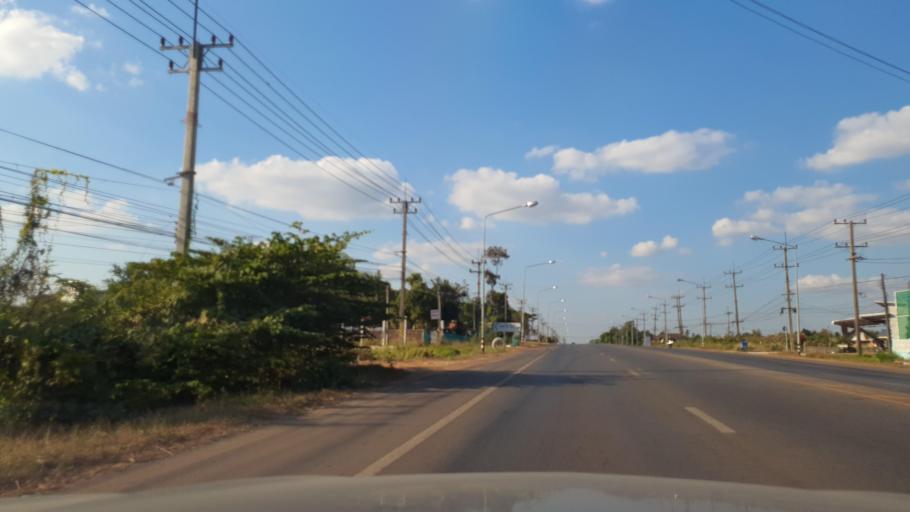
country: TH
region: Sakon Nakhon
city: Sakon Nakhon
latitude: 17.1634
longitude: 104.1018
